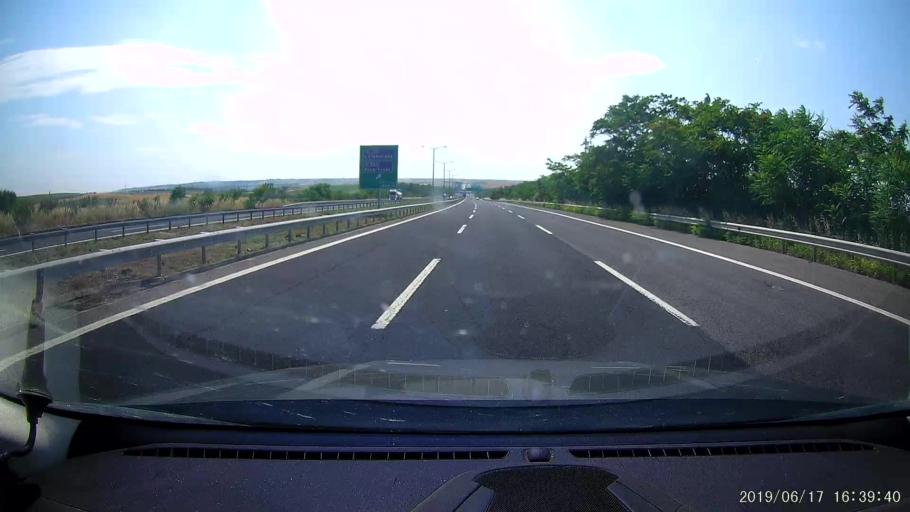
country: TR
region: Kirklareli
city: Luleburgaz
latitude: 41.4501
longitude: 27.4036
